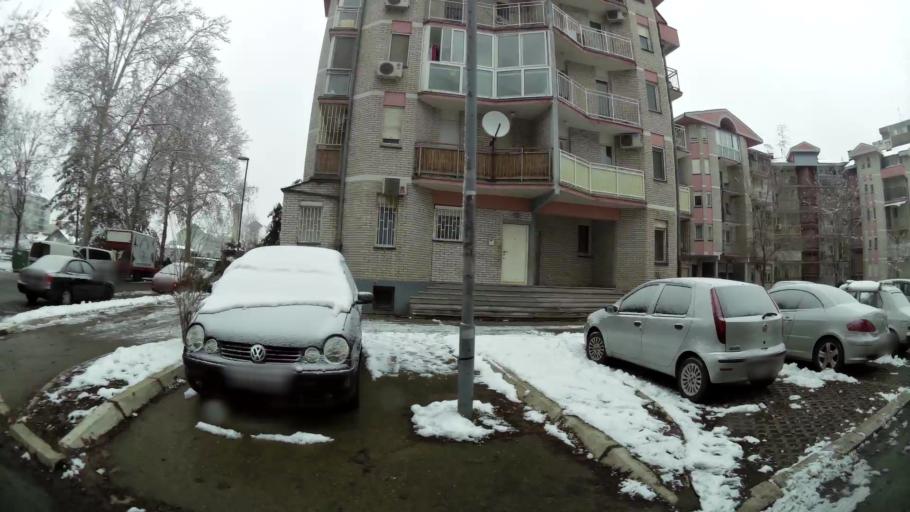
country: RS
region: Central Serbia
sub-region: Belgrade
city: Zemun
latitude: 44.8333
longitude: 20.4149
